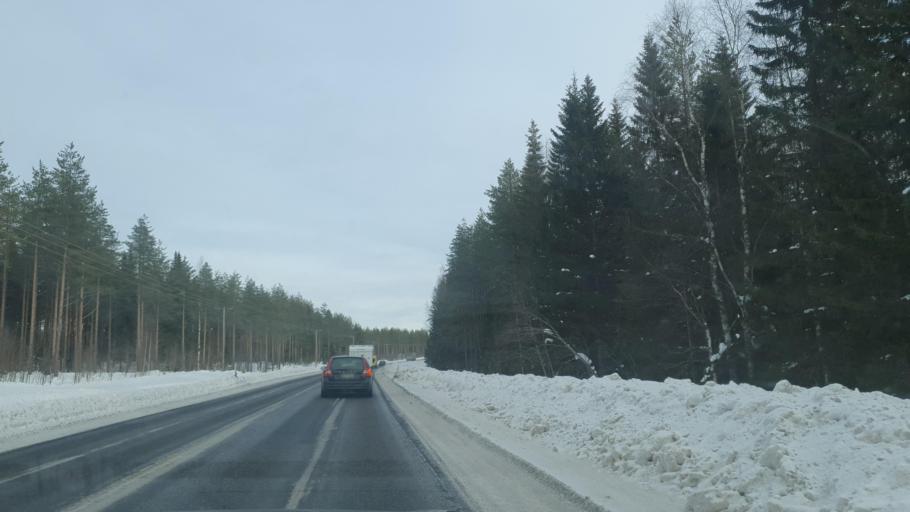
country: FI
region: Kainuu
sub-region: Kajaani
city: Paltamo
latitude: 64.4267
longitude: 27.5981
